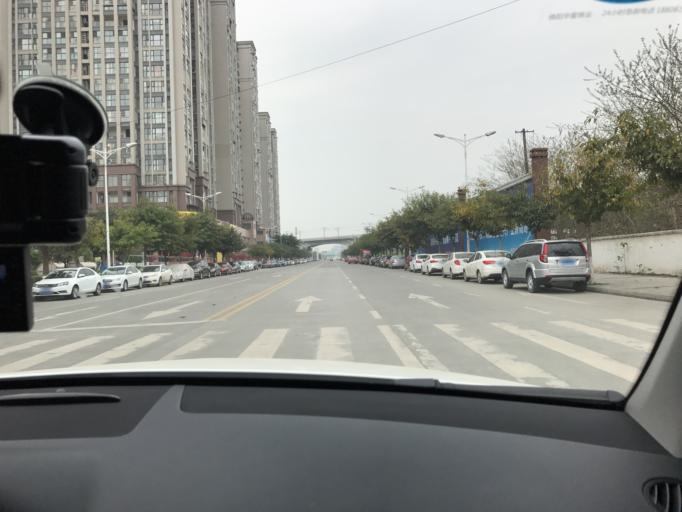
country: CN
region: Sichuan
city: Mianyang
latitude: 31.4587
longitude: 104.6868
